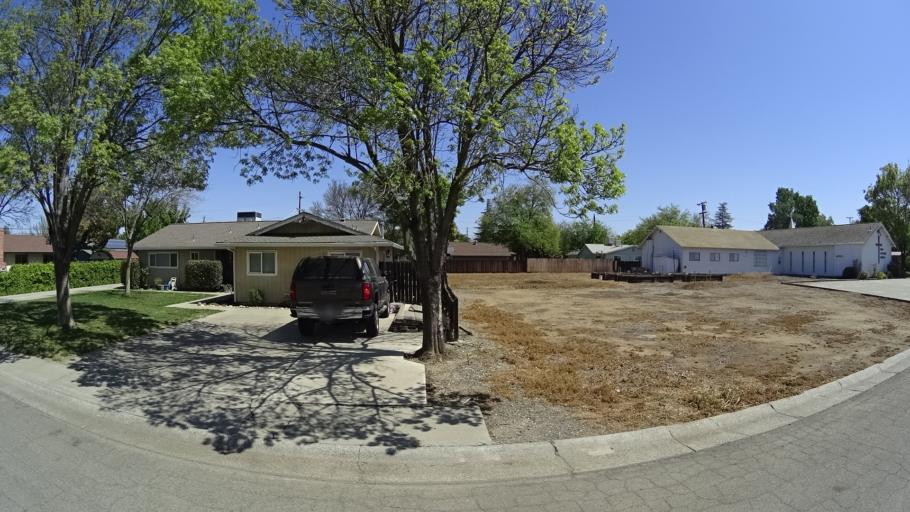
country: US
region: California
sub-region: Glenn County
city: Willows
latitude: 39.5261
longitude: -122.1982
